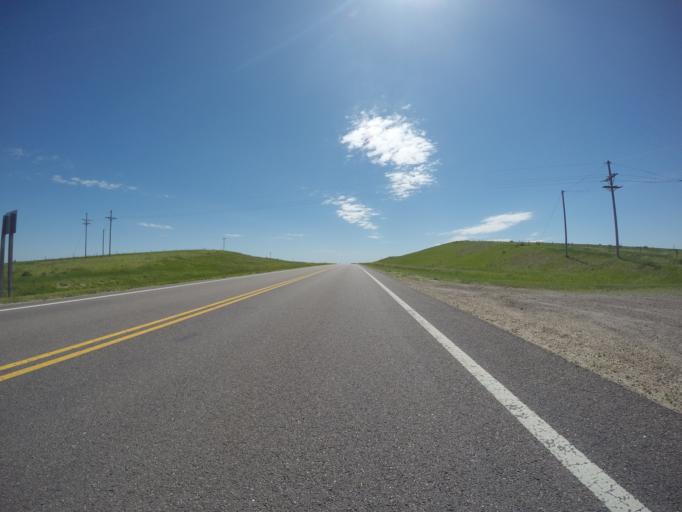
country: US
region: Kansas
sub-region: Rawlins County
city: Atwood
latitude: 39.8134
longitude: -101.0254
